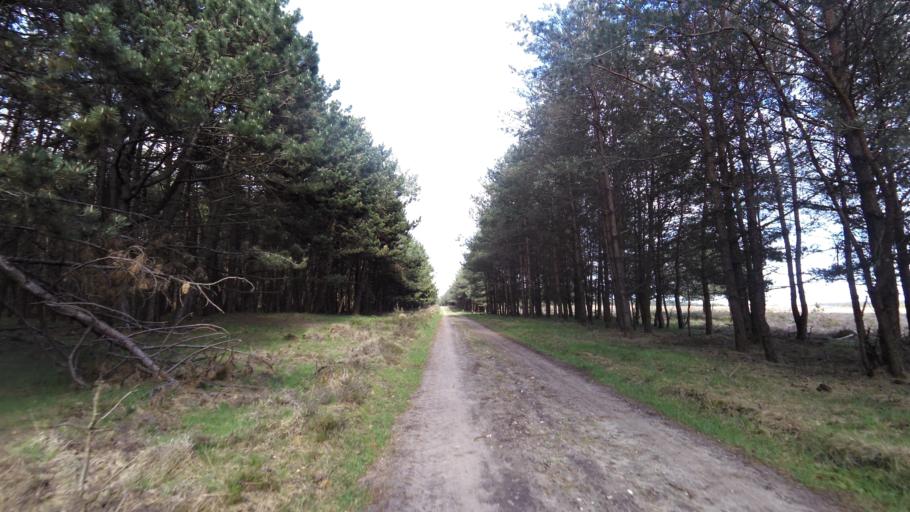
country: NL
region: Gelderland
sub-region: Gemeente Rozendaal
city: Rozendaal
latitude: 52.0618
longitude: 5.9609
